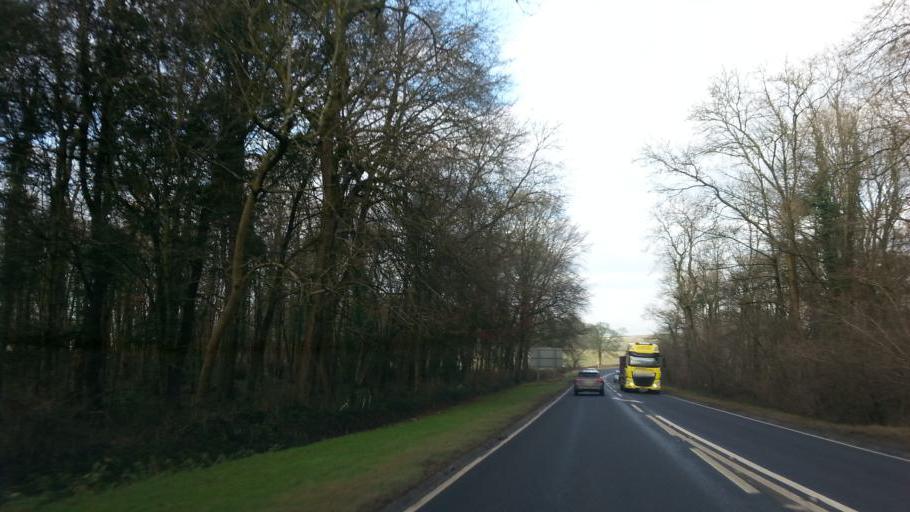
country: GB
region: England
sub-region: South Gloucestershire
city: Hinton
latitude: 51.4822
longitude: -2.3620
